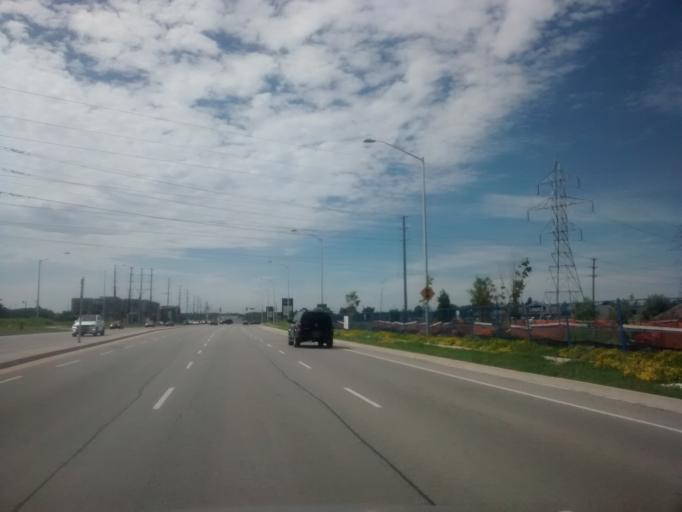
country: CA
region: Ontario
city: Burlington
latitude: 43.4090
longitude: -79.8110
